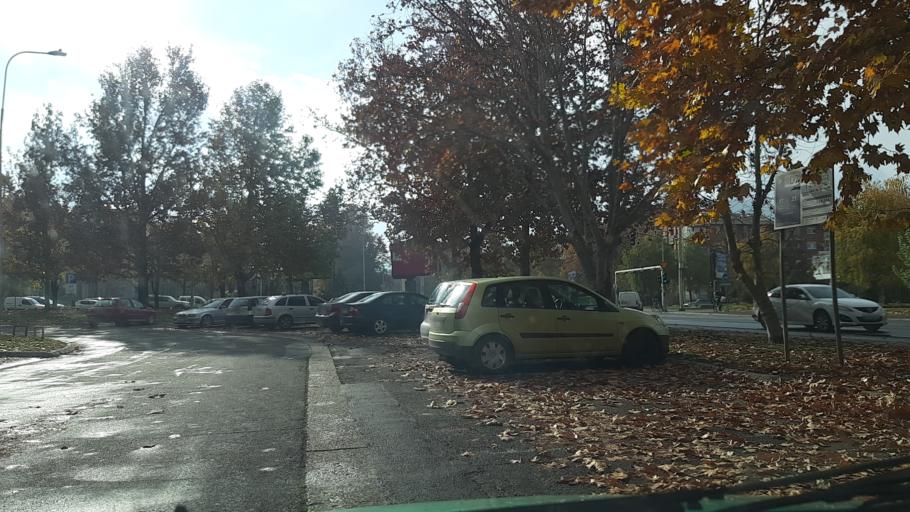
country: MK
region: Kisela Voda
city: Usje
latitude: 41.9884
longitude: 21.4629
